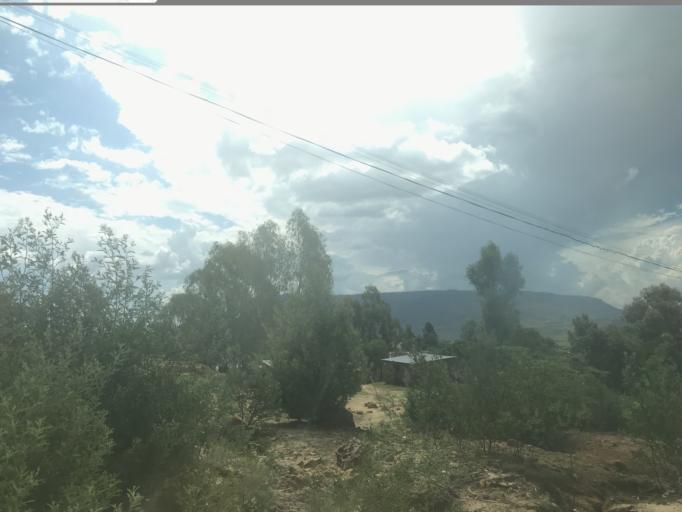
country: LS
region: Maseru
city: Nako
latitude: -29.6288
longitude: 27.5129
